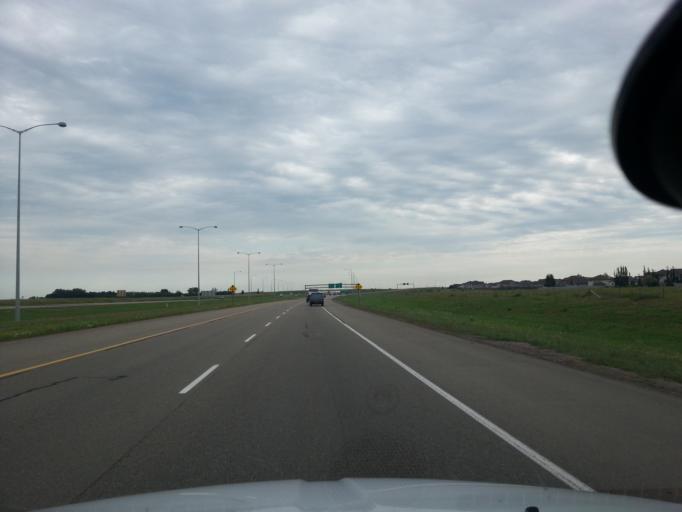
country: CA
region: Alberta
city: Edmonton
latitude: 53.6465
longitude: -113.5115
